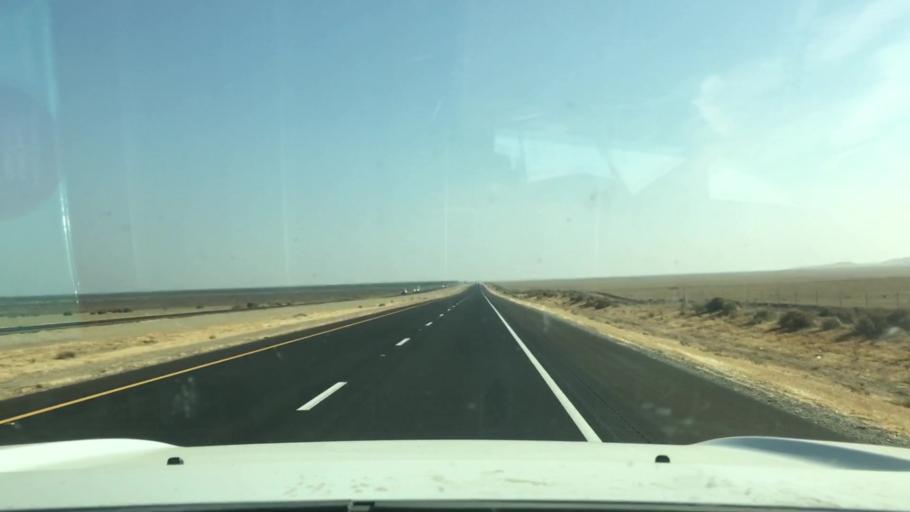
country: US
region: California
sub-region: Kern County
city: Lost Hills
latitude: 35.6271
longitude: -119.9913
